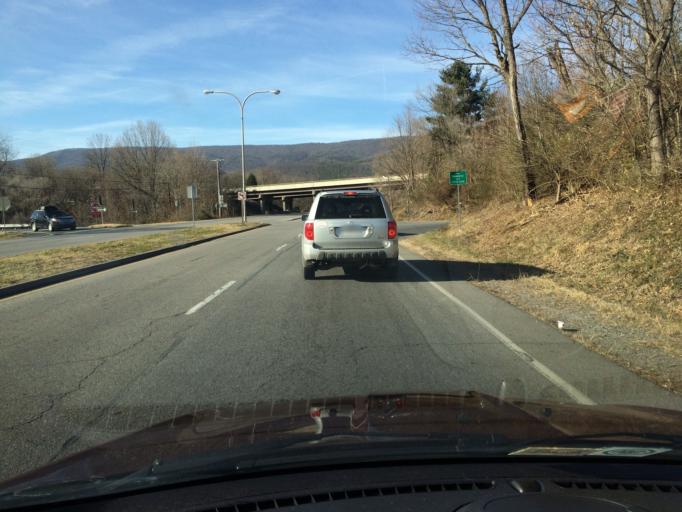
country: US
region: Virginia
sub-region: City of Salem
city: Salem
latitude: 37.2925
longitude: -80.0982
